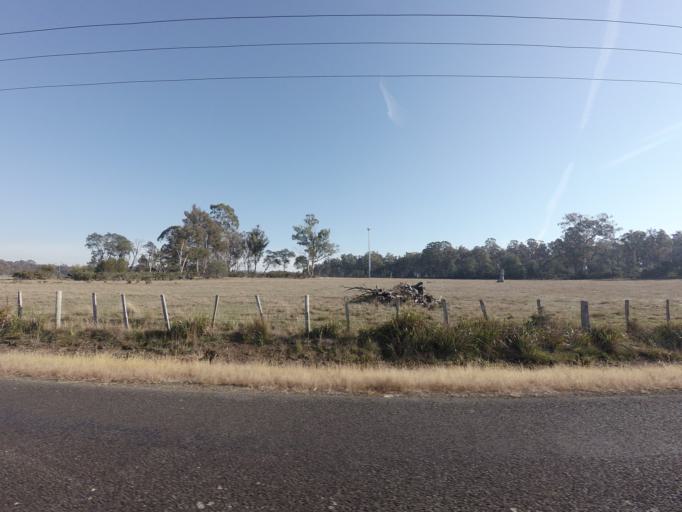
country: AU
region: Tasmania
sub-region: Northern Midlands
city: Longford
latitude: -41.5347
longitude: 146.9968
